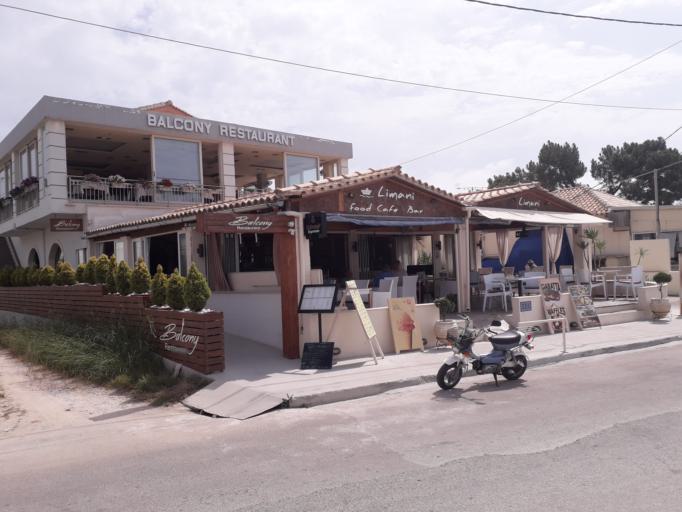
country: GR
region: Ionian Islands
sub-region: Nomos Kerkyras
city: Perivoli
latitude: 39.4269
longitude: 19.9437
